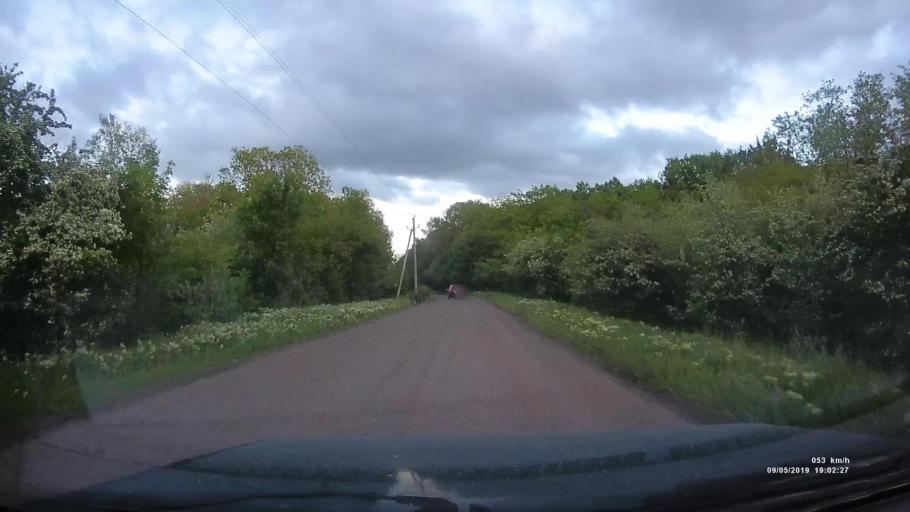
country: RU
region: Krasnodarskiy
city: Kanelovskaya
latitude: 46.7449
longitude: 39.1533
